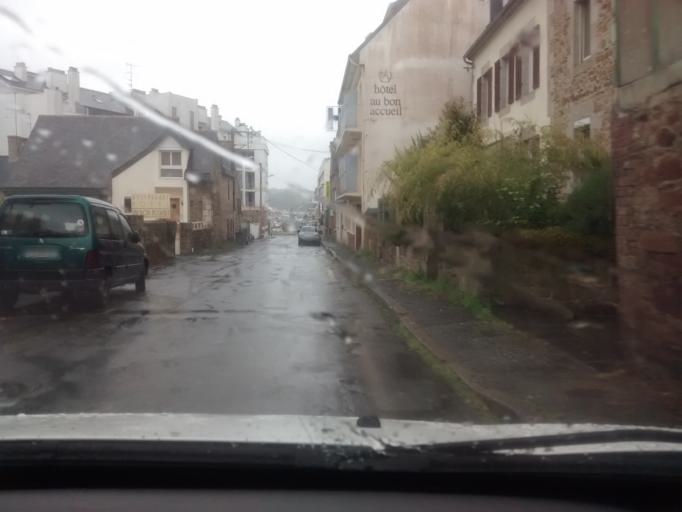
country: FR
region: Brittany
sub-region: Departement des Cotes-d'Armor
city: Perros-Guirec
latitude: 48.8049
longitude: -3.4439
